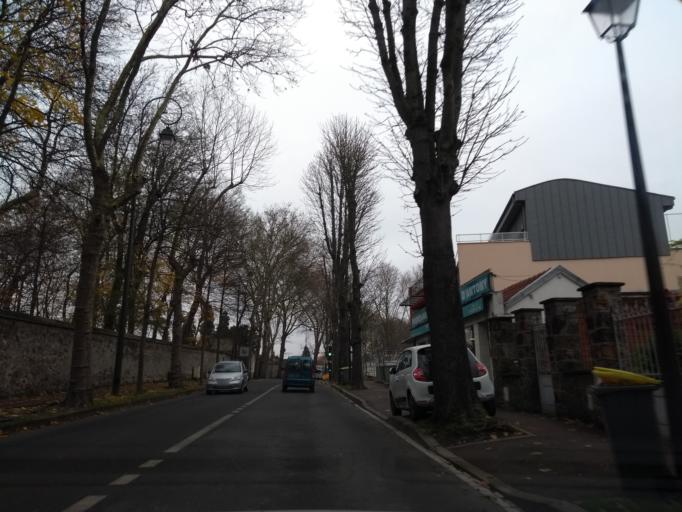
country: FR
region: Ile-de-France
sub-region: Departement des Hauts-de-Seine
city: Antony
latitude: 48.7578
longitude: 2.2925
